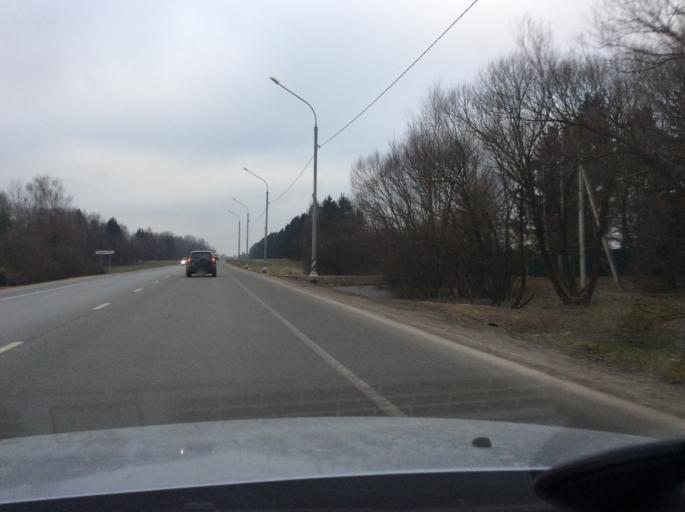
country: RU
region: Moskovskaya
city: Troitsk
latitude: 55.3679
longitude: 37.2002
